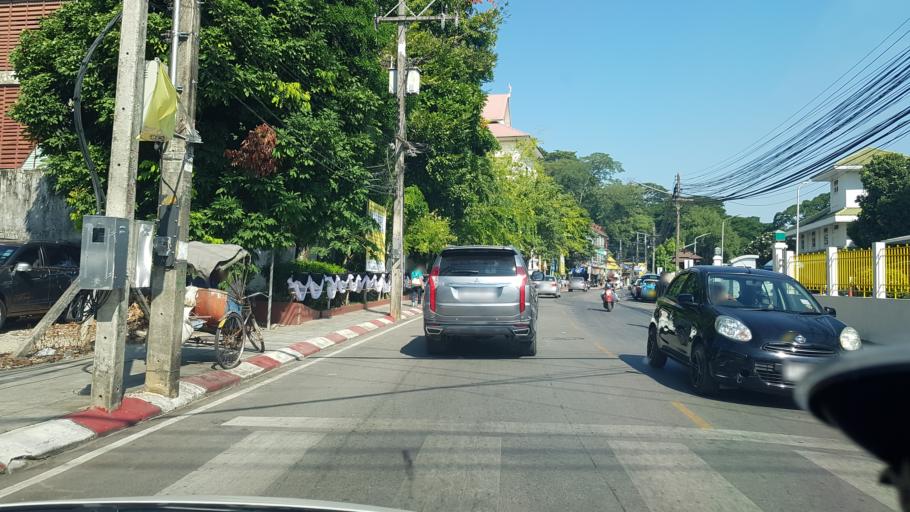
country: TH
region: Chiang Rai
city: Chiang Rai
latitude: 19.9111
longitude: 99.8281
